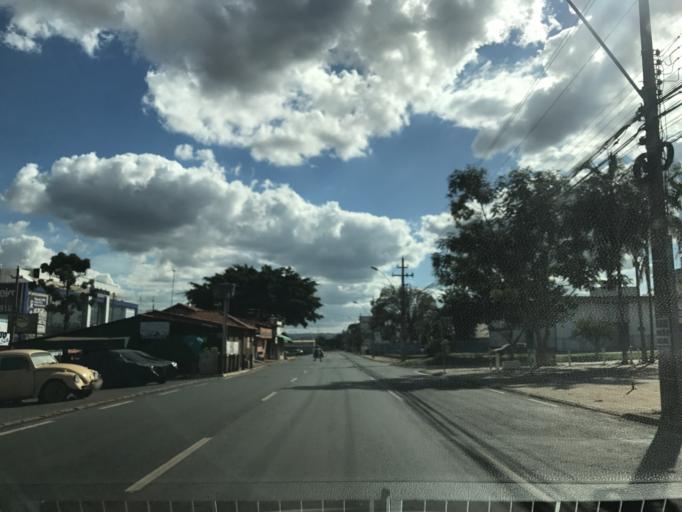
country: BR
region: Federal District
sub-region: Brasilia
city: Brasilia
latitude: -15.8030
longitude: -47.9647
